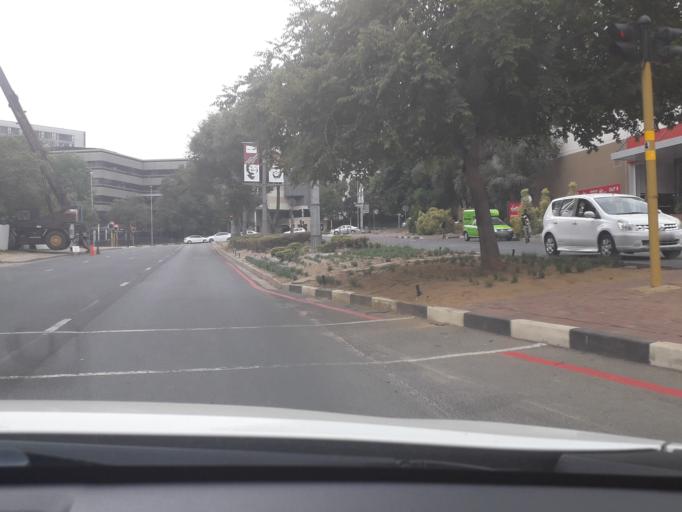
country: ZA
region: Gauteng
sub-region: City of Johannesburg Metropolitan Municipality
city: Johannesburg
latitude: -26.1053
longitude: 28.0532
